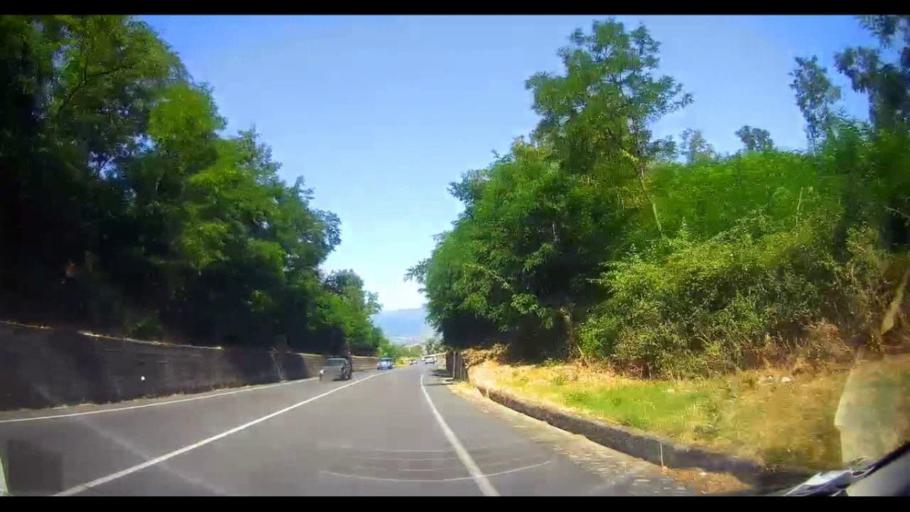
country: IT
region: Calabria
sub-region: Provincia di Cosenza
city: Zumpano
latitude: 39.2985
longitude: 16.2932
